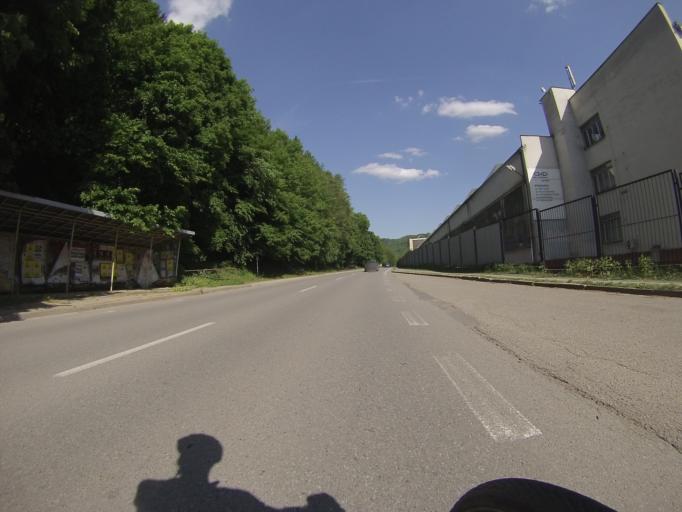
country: CZ
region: South Moravian
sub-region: Okres Blansko
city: Blansko
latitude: 49.3534
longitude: 16.6737
